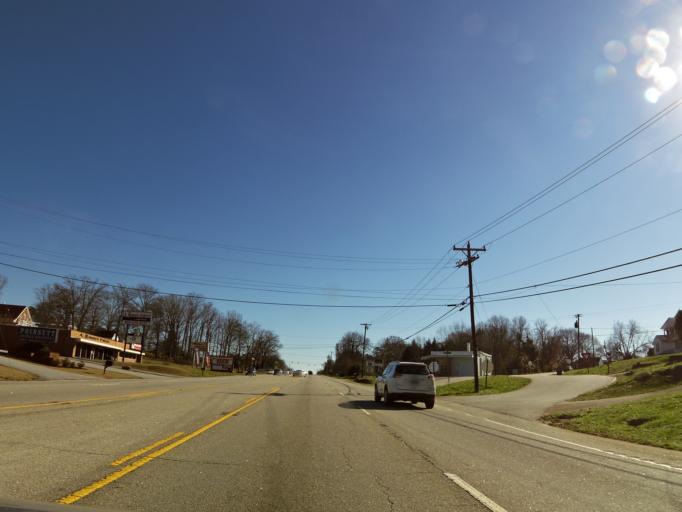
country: US
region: South Carolina
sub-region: Greenville County
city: Sans Souci
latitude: 34.9005
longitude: -82.4155
